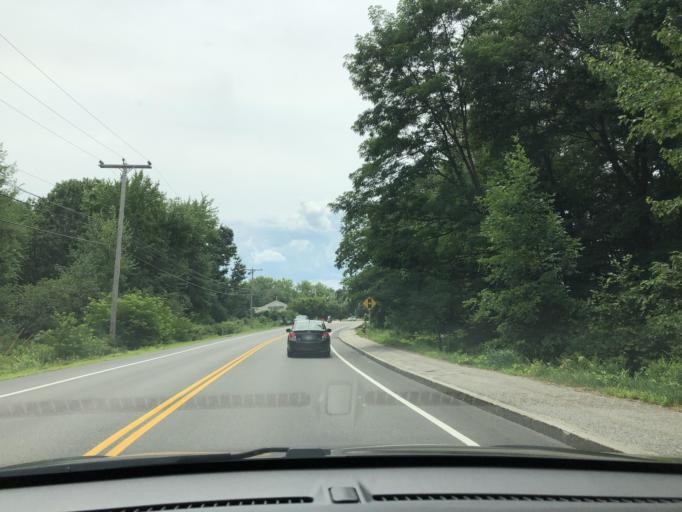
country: US
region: New Hampshire
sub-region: Merrimack County
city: Concord
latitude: 43.1951
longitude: -71.5195
